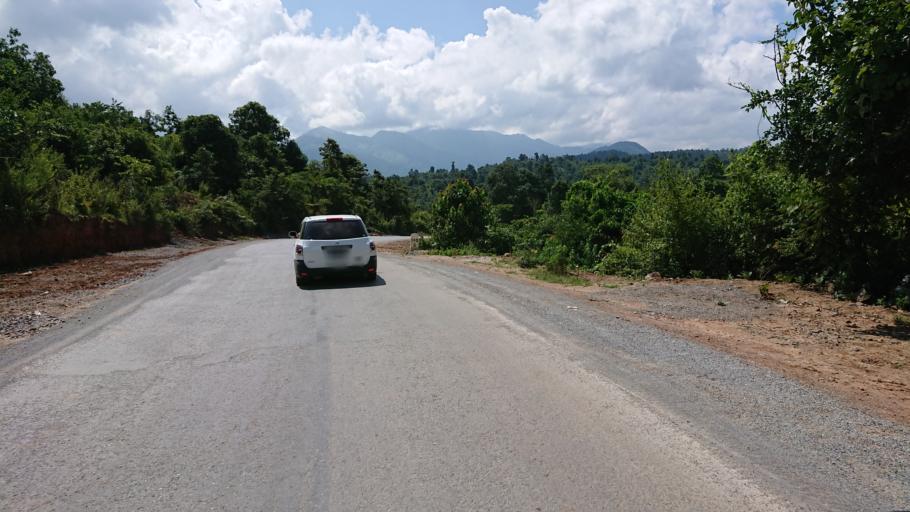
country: MM
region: Shan
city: Taunggyi
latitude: 20.8146
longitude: 97.3174
